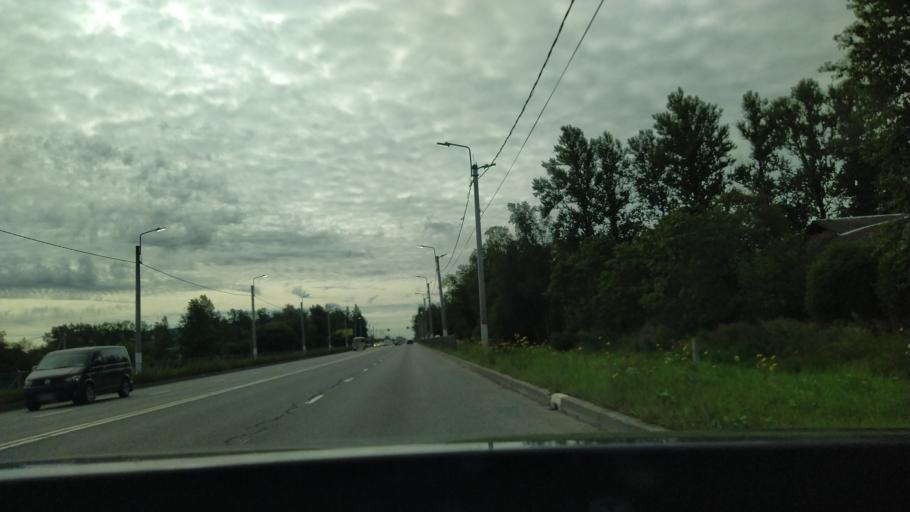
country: RU
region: Leningrad
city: Tosno
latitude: 59.5608
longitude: 30.8407
